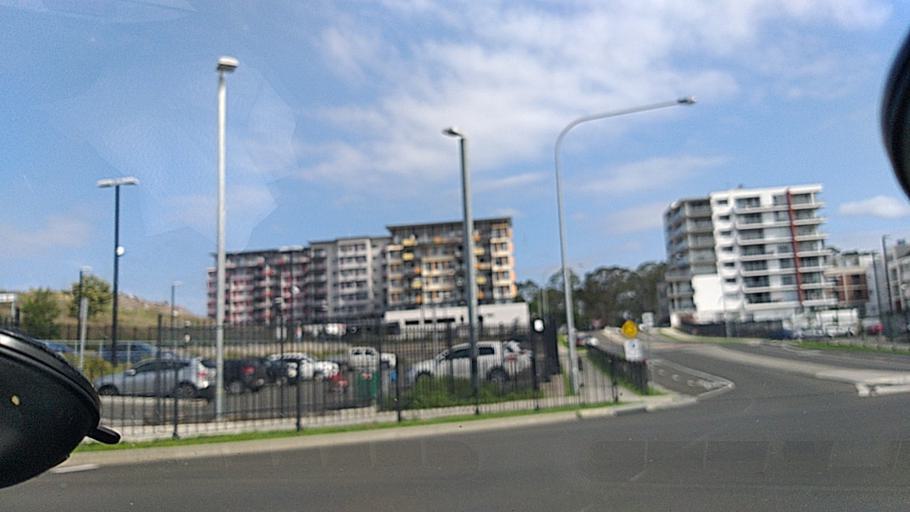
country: AU
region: New South Wales
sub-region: Campbelltown Municipality
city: Glen Alpine
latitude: -34.0731
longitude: 150.7931
